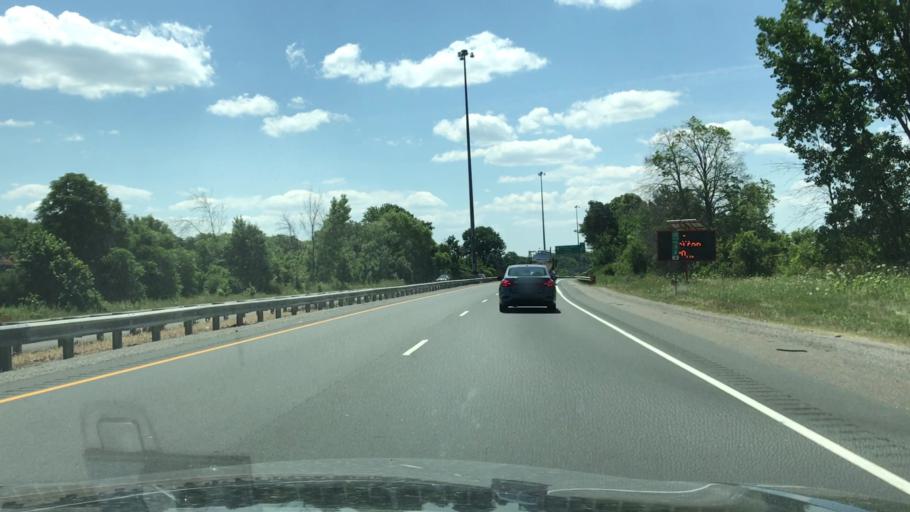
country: CA
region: Ontario
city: Niagara Falls
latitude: 43.1218
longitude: -79.1210
